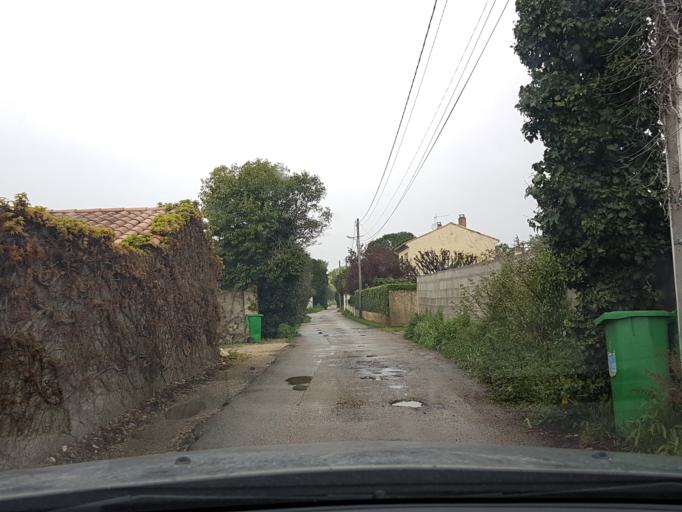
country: FR
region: Provence-Alpes-Cote d'Azur
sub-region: Departement du Vaucluse
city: Sorgues
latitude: 43.9855
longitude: 4.8730
